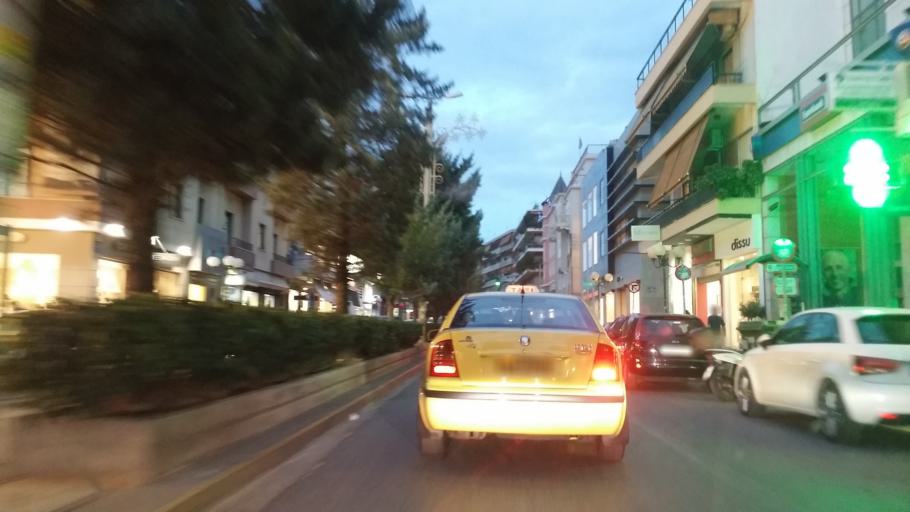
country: GR
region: Attica
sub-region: Nomarchia Athinas
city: Nea Ionia
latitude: 38.0452
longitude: 23.7571
